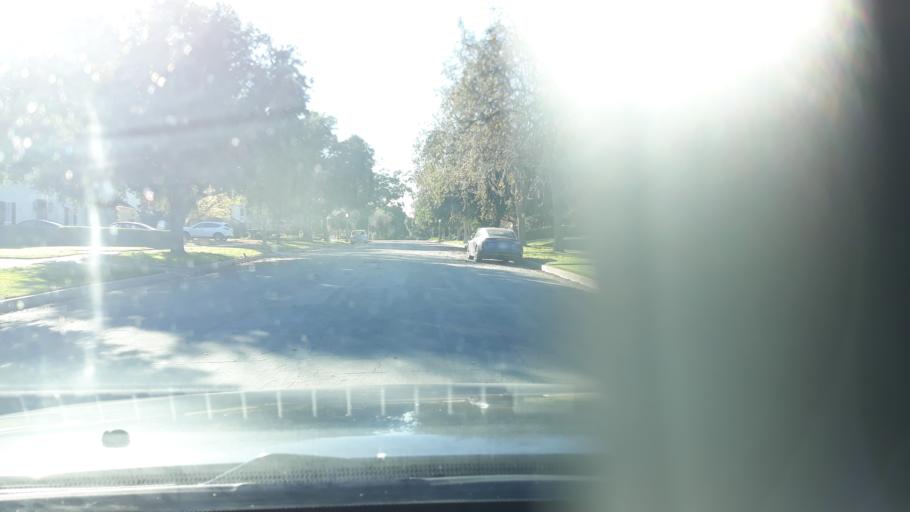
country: US
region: California
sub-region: Los Angeles County
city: San Marino
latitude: 34.1218
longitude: -118.1023
